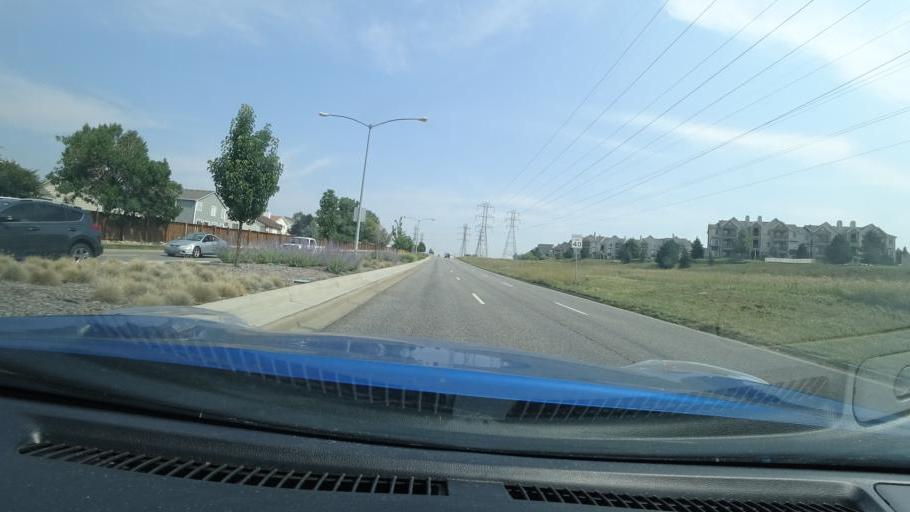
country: US
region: Colorado
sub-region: Adams County
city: Aurora
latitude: 39.6787
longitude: -104.7724
